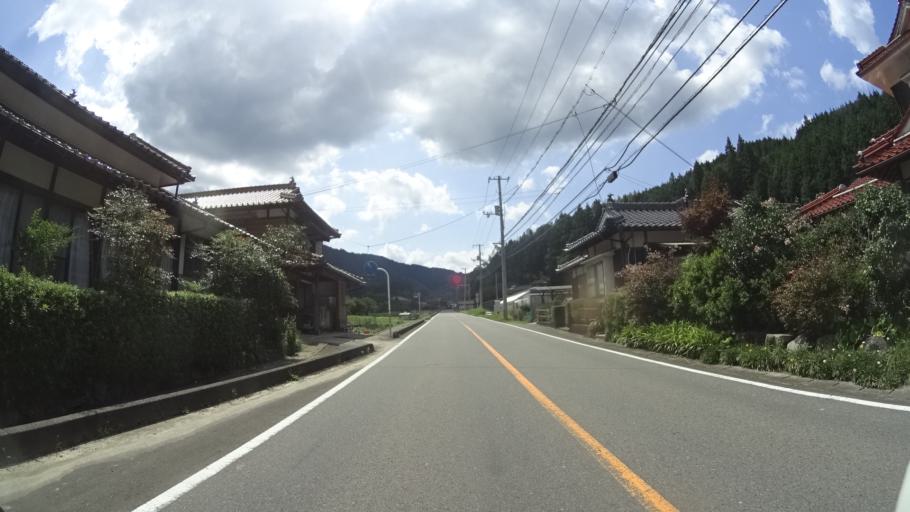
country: JP
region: Yamaguchi
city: Hagi
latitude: 34.4347
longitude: 131.4784
